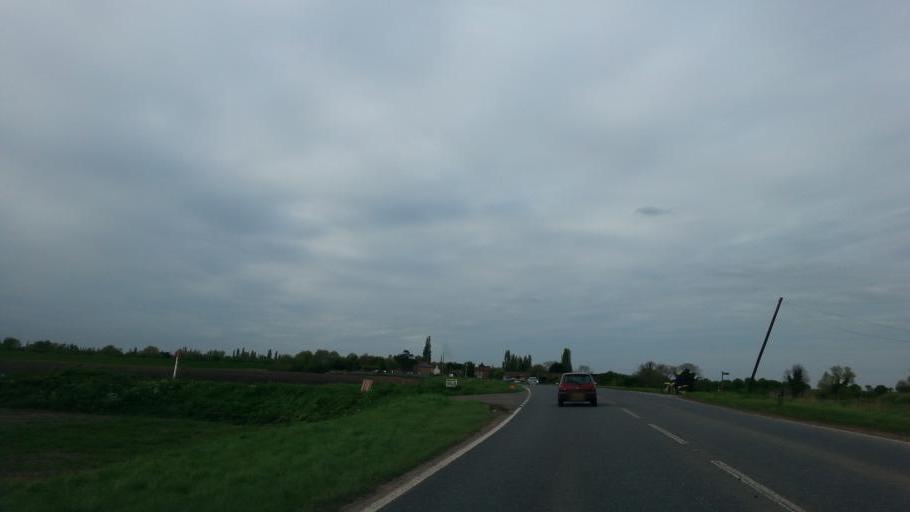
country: GB
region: England
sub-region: Cambridgeshire
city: March
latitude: 52.5986
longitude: 0.0619
